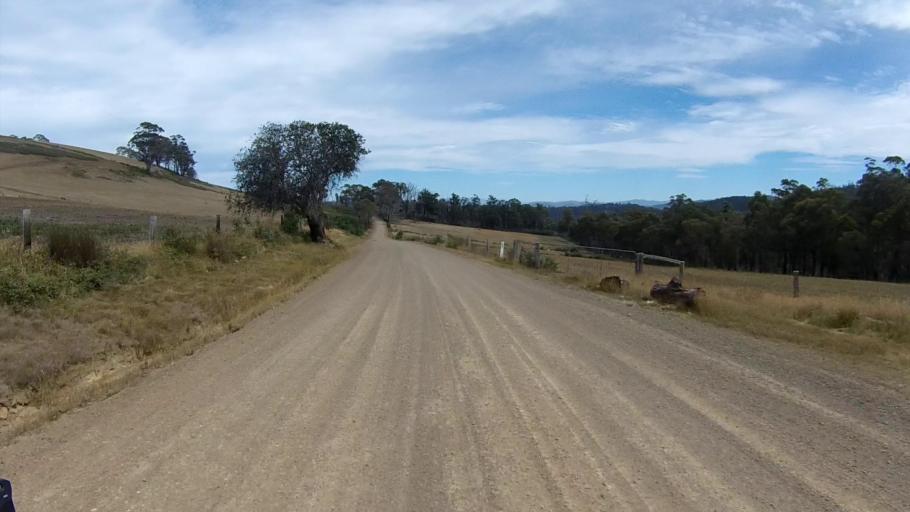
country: AU
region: Tasmania
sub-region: Sorell
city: Sorell
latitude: -42.7887
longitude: 147.7074
